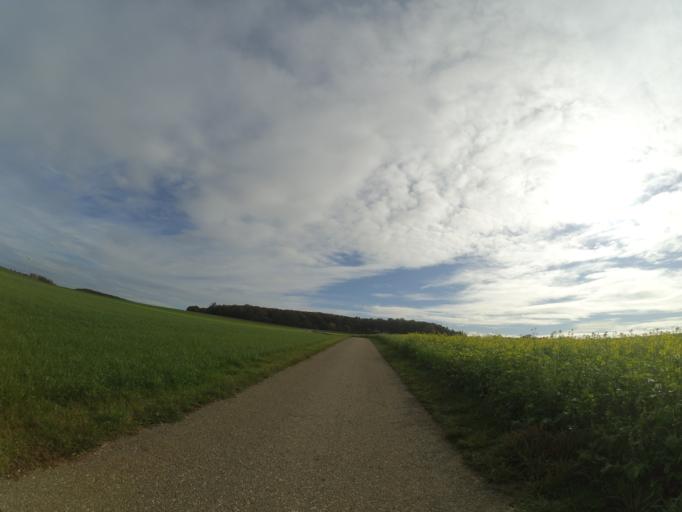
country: DE
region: Baden-Wuerttemberg
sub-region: Tuebingen Region
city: Lonsee
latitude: 48.5529
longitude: 9.9228
